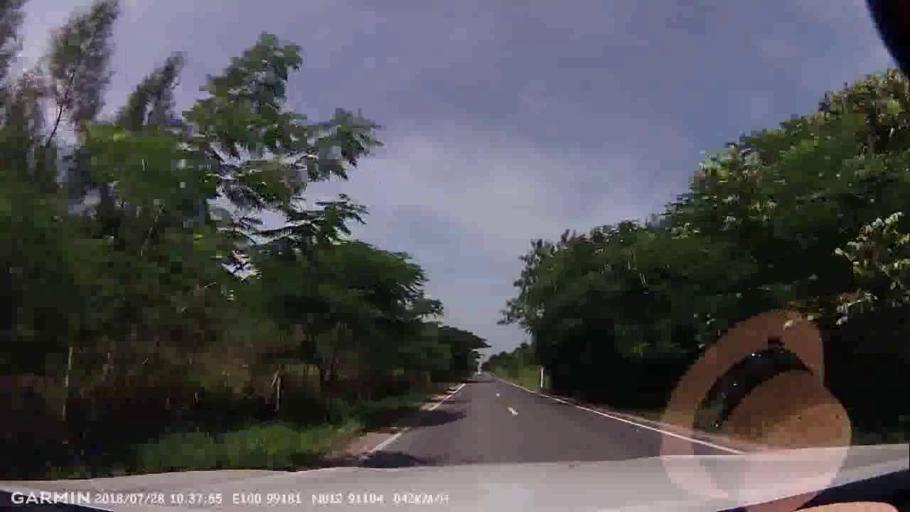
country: TH
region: Chon Buri
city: Phatthaya
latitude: 12.9109
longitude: 100.9918
